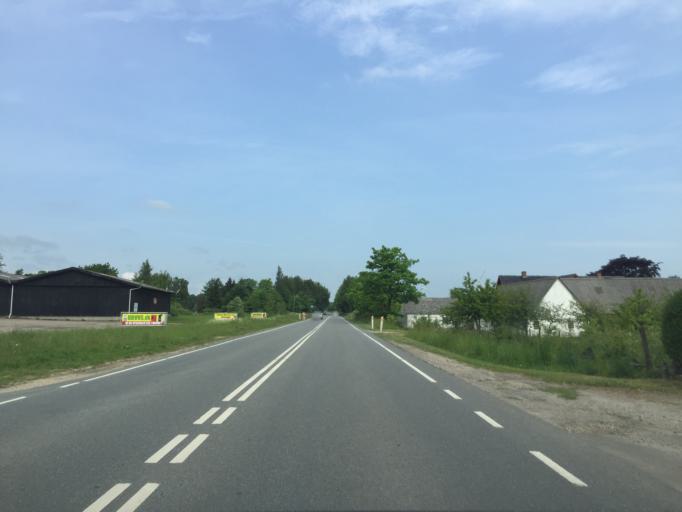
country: DK
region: South Denmark
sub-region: Nyborg Kommune
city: Nyborg
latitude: 55.1889
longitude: 10.7325
